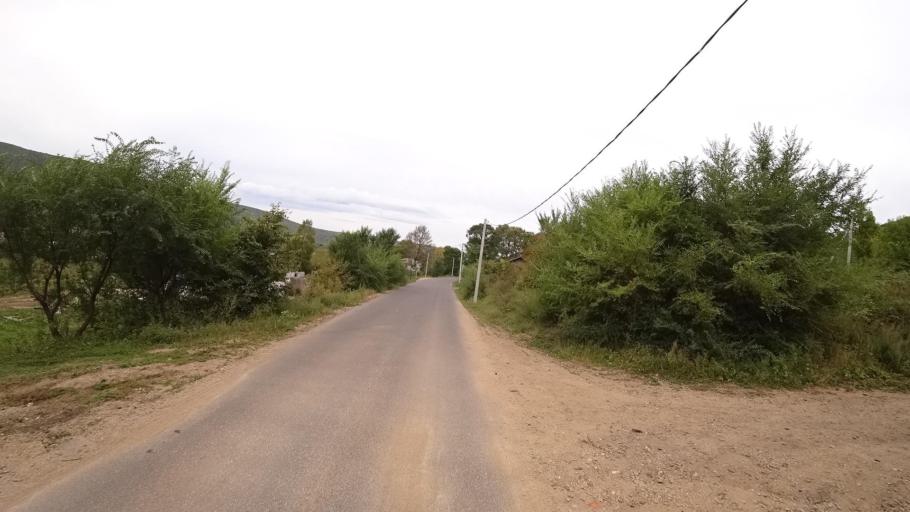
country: RU
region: Jewish Autonomous Oblast
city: Khingansk
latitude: 49.0302
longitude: 131.0583
